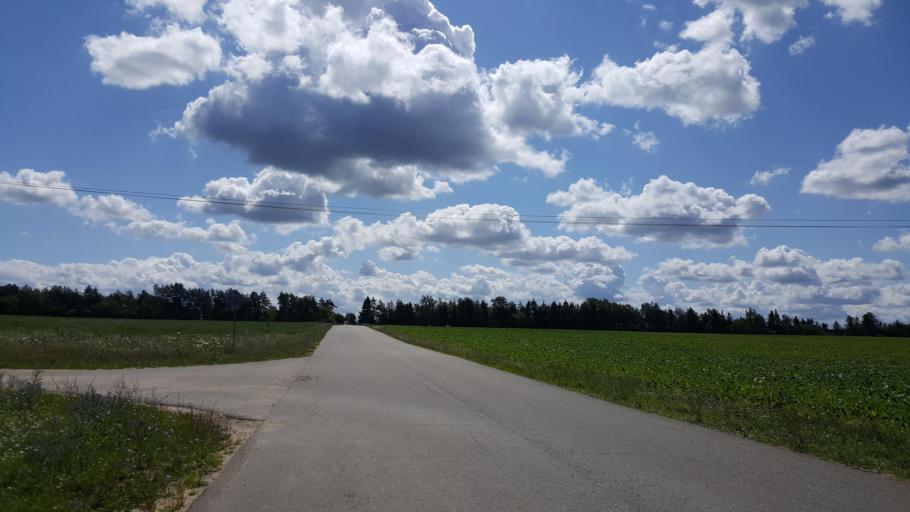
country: BY
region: Brest
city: Kamyanyets
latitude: 52.3844
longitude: 23.8054
